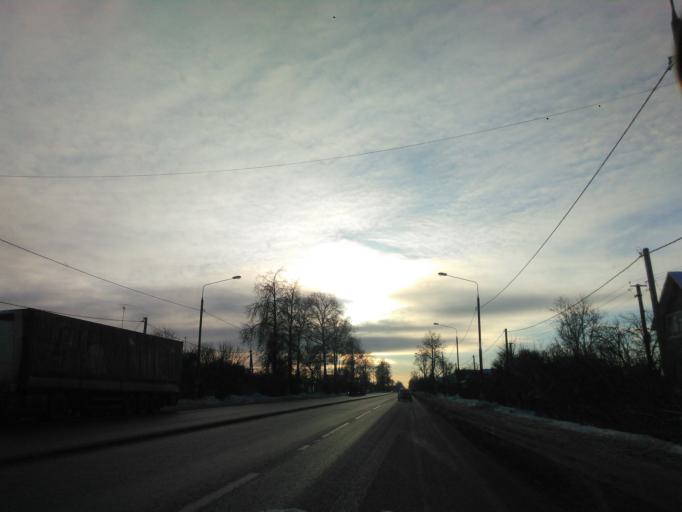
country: RU
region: Moskovskaya
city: Spas-Zaulok
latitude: 56.4872
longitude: 36.5647
